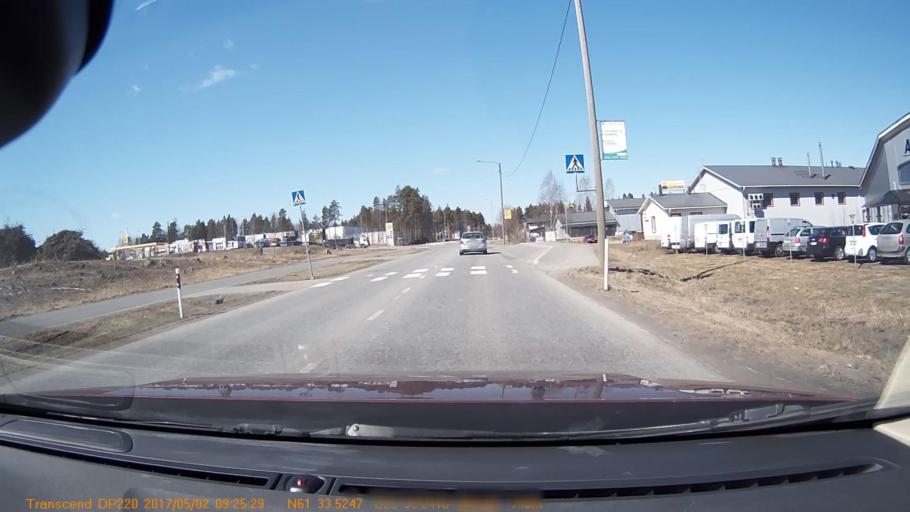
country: FI
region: Pirkanmaa
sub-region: Tampere
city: Yloejaervi
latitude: 61.5587
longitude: 23.5538
